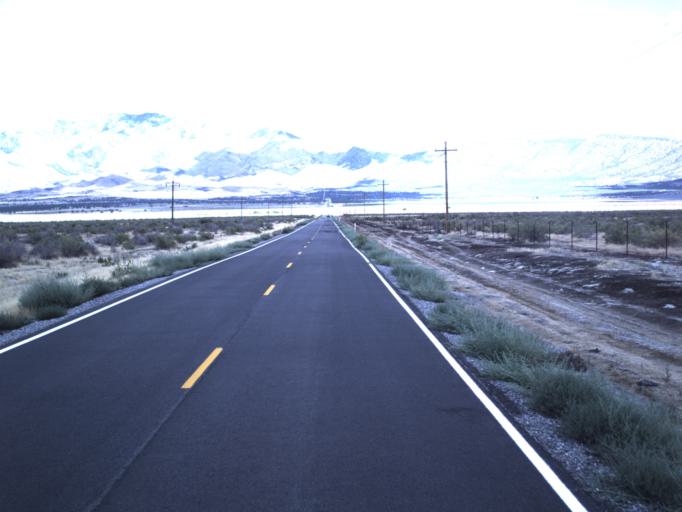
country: US
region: Utah
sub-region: Tooele County
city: Grantsville
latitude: 40.2777
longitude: -112.6737
